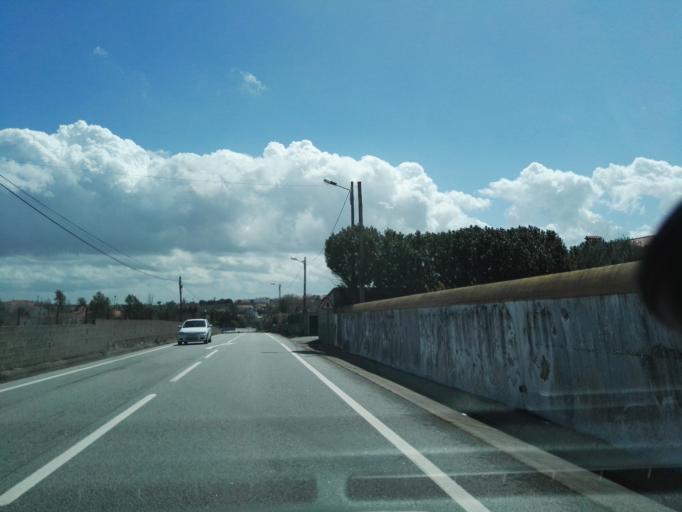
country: PT
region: Portalegre
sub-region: Arronches
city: Arronches
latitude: 39.1291
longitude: -7.2844
